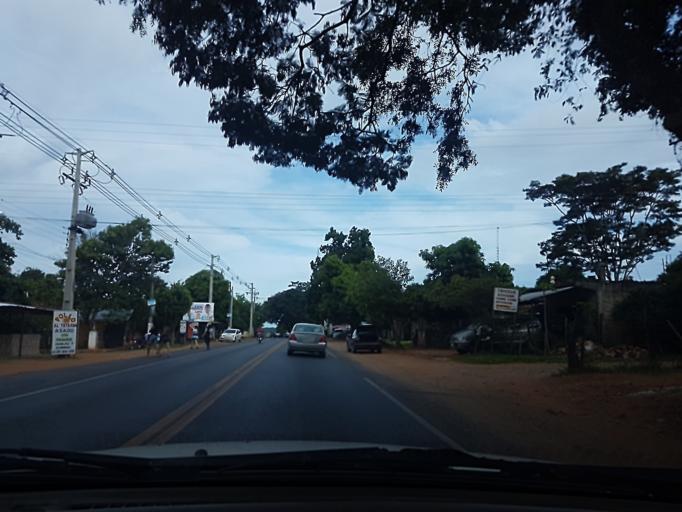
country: PY
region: Central
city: Capiata
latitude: -25.2883
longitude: -57.4589
